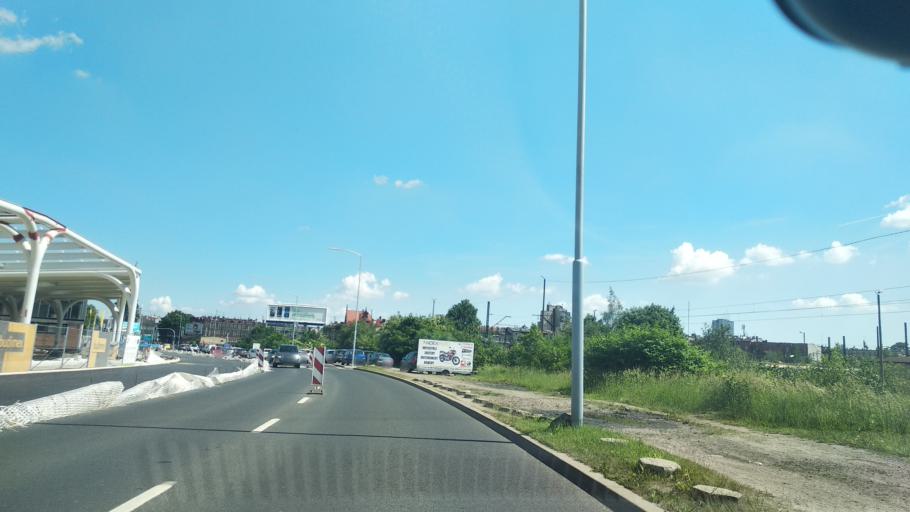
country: PL
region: Silesian Voivodeship
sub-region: Katowice
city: Katowice
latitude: 50.2592
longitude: 19.0092
